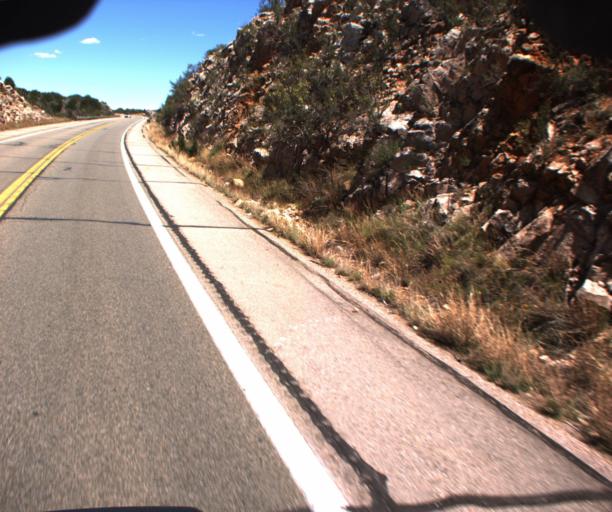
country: US
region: Arizona
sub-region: Yavapai County
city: Paulden
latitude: 34.9310
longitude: -112.4412
